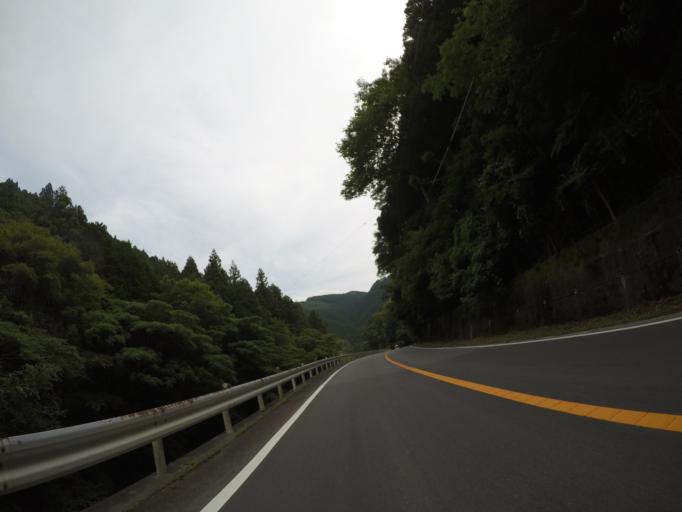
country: JP
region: Shizuoka
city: Fujinomiya
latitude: 35.1993
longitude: 138.5394
